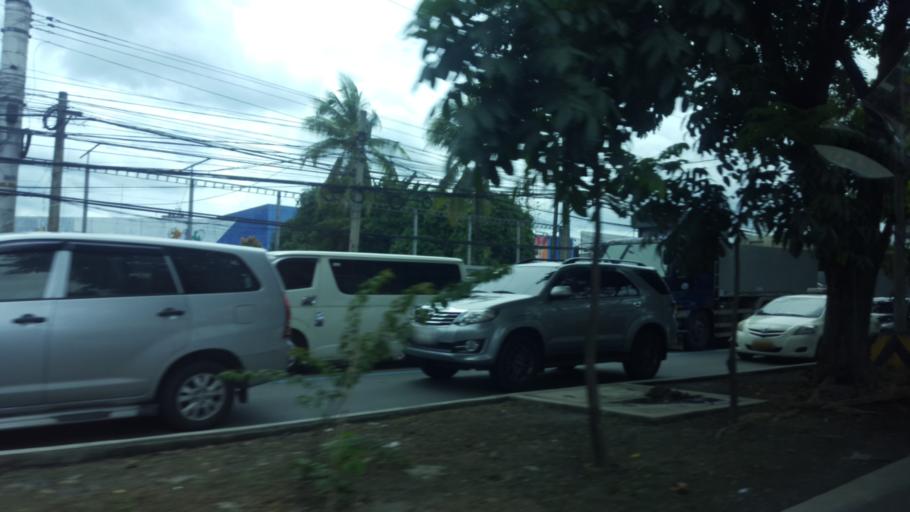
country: PH
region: Metro Manila
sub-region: Marikina
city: Calumpang
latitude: 14.6047
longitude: 121.0791
